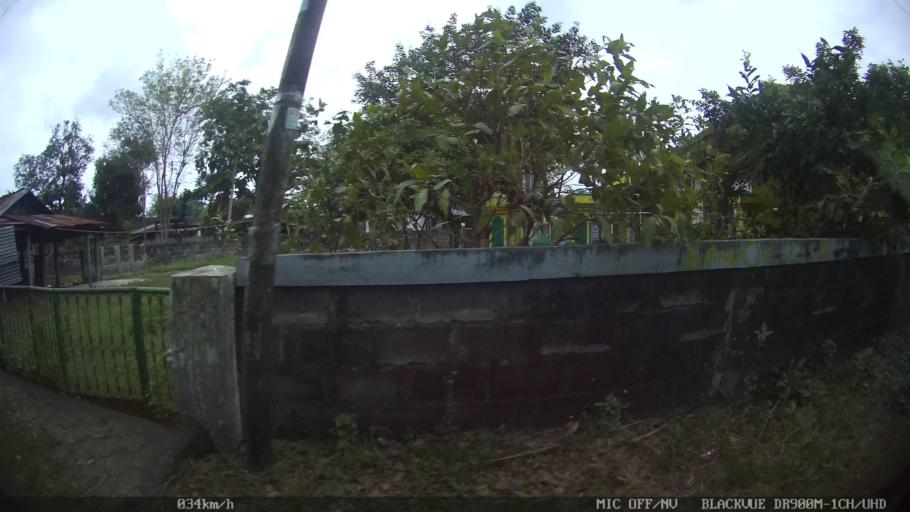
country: ID
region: Daerah Istimewa Yogyakarta
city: Sewon
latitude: -7.8768
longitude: 110.4169
